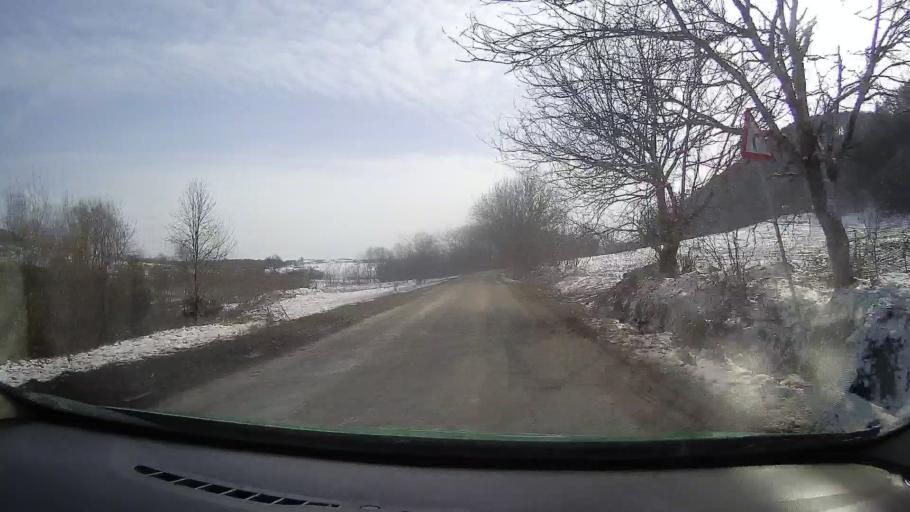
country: RO
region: Mures
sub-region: Comuna Apold
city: Saes
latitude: 46.1935
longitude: 24.7647
